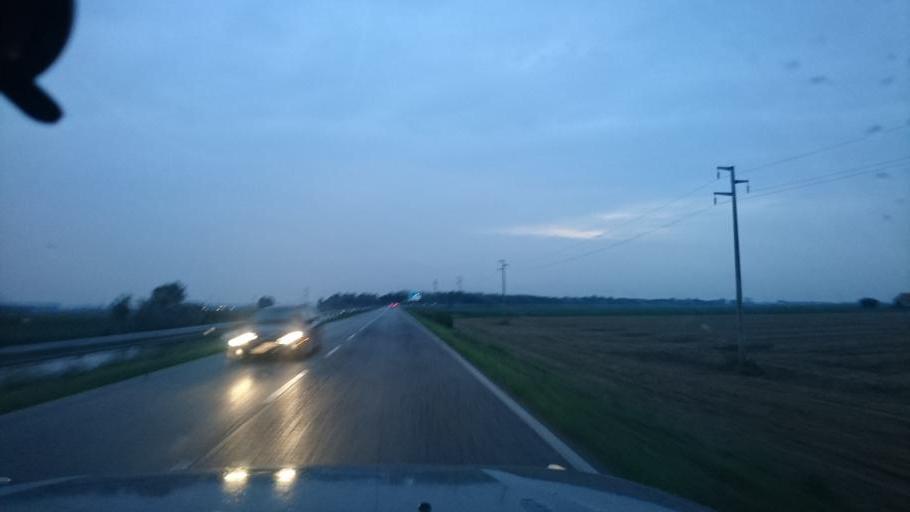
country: IT
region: Emilia-Romagna
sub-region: Provincia di Ferrara
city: Mesola
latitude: 44.9465
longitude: 12.2672
